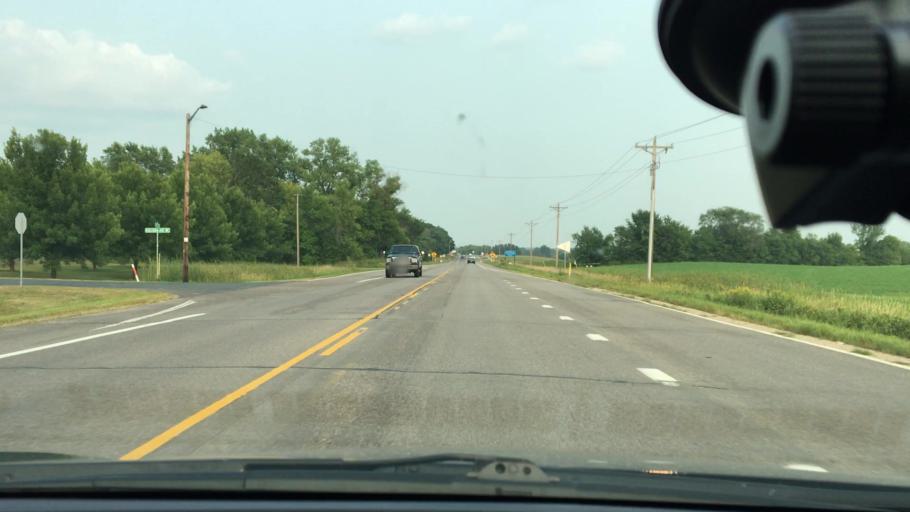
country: US
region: Minnesota
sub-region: Wright County
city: Albertville
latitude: 45.2894
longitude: -93.6701
